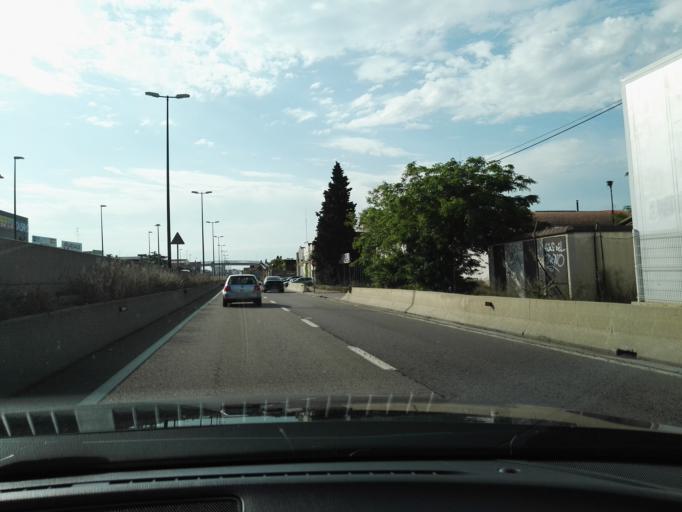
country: ES
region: Aragon
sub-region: Provincia de Zaragoza
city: Zaragoza
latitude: 41.6269
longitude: -0.8507
